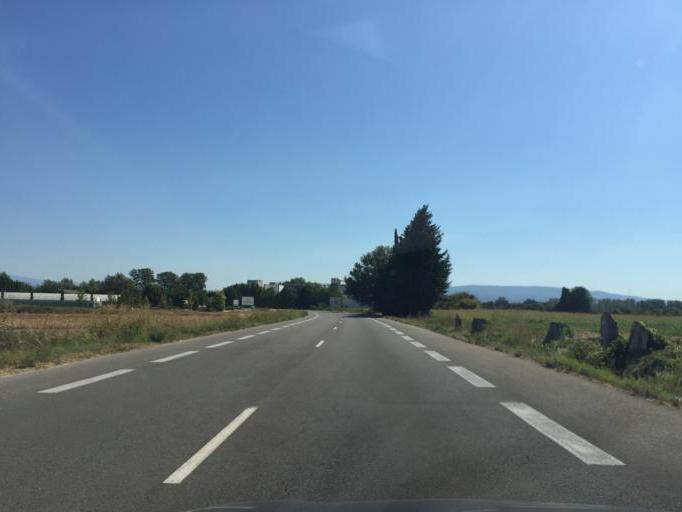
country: FR
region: Provence-Alpes-Cote d'Azur
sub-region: Departement du Vaucluse
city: Althen-des-Paluds
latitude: 43.9662
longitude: 4.9730
